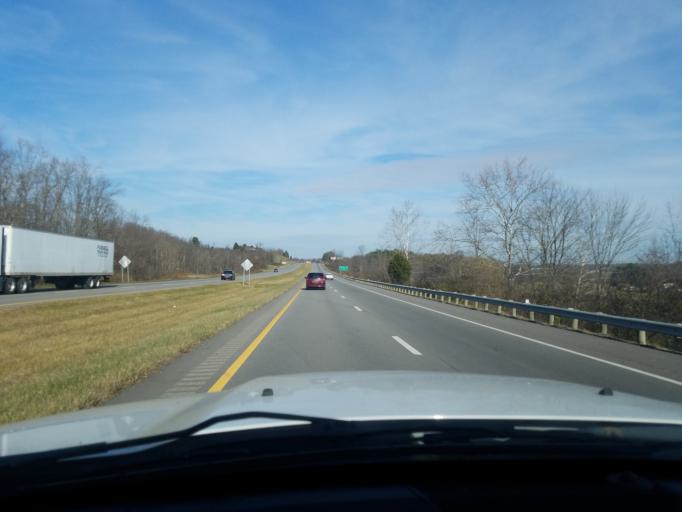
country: US
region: Ohio
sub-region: Athens County
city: Athens
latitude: 39.2660
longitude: -82.1627
